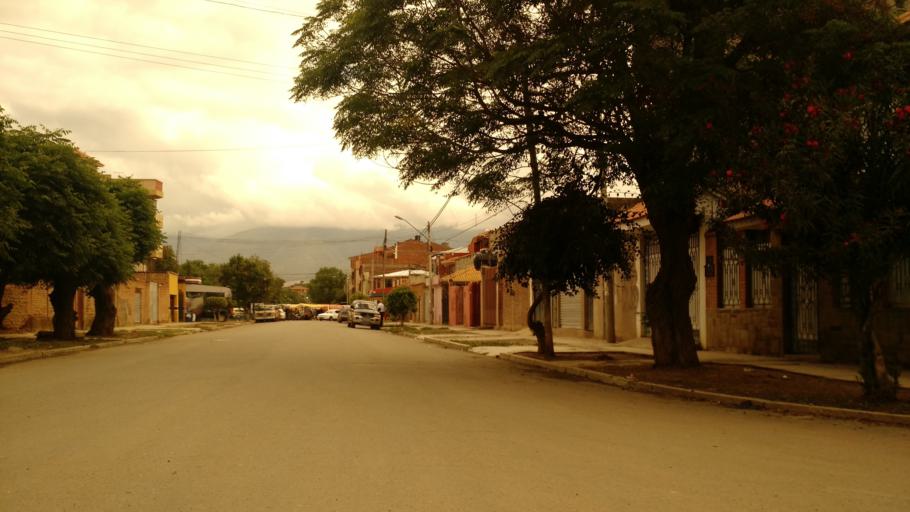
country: BO
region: Cochabamba
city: Cochabamba
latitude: -17.4227
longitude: -66.1574
